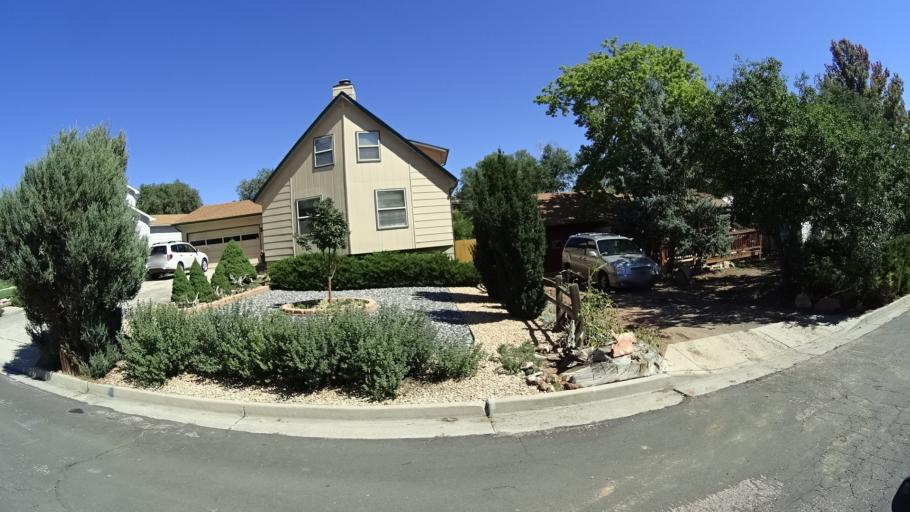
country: US
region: Colorado
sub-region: El Paso County
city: Colorado Springs
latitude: 38.8531
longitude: -104.8578
